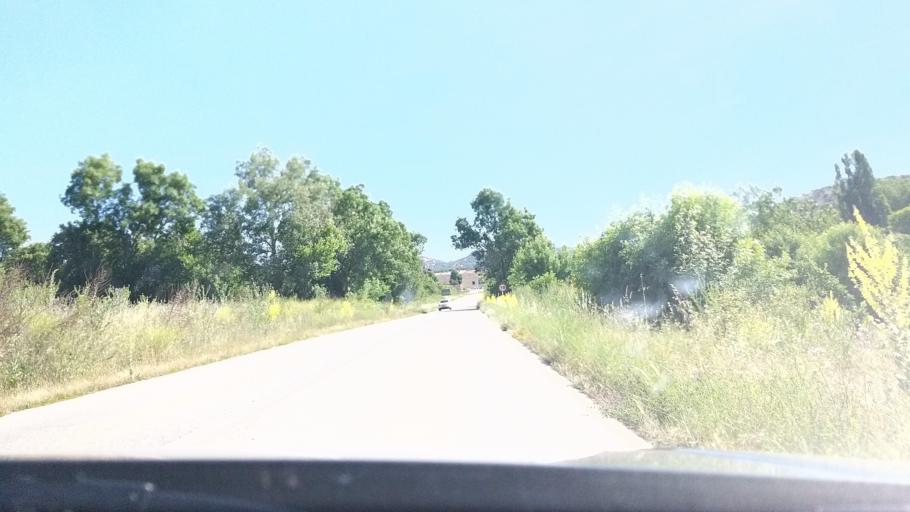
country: ES
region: Castille and Leon
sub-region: Provincia de Segovia
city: Pedraza
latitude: 41.1402
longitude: -3.8310
